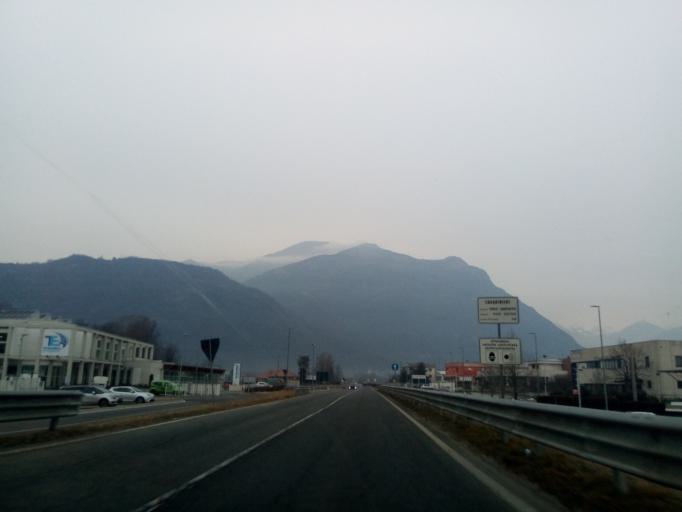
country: IT
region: Piedmont
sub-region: Provincia di Torino
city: Fiorano Canavese
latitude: 45.4752
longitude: 7.8341
